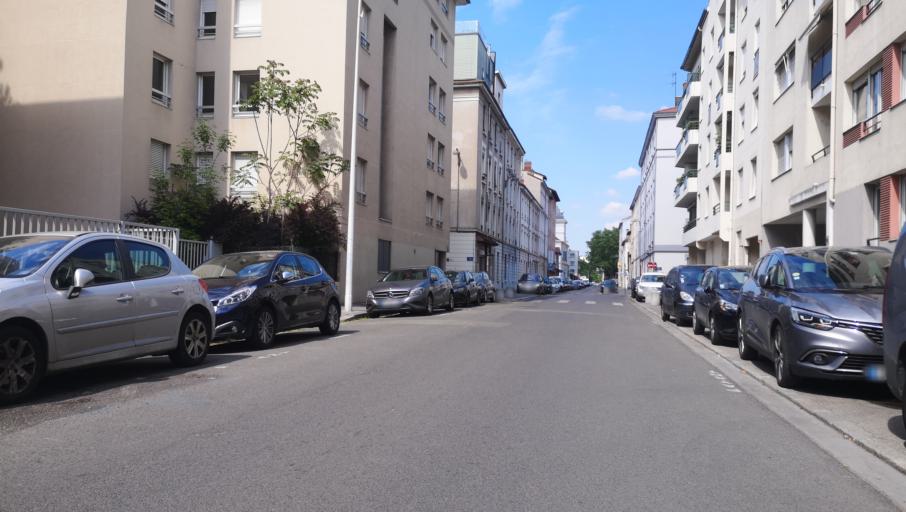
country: FR
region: Rhone-Alpes
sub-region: Departement du Rhone
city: Lyon
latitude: 45.7438
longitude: 4.8655
